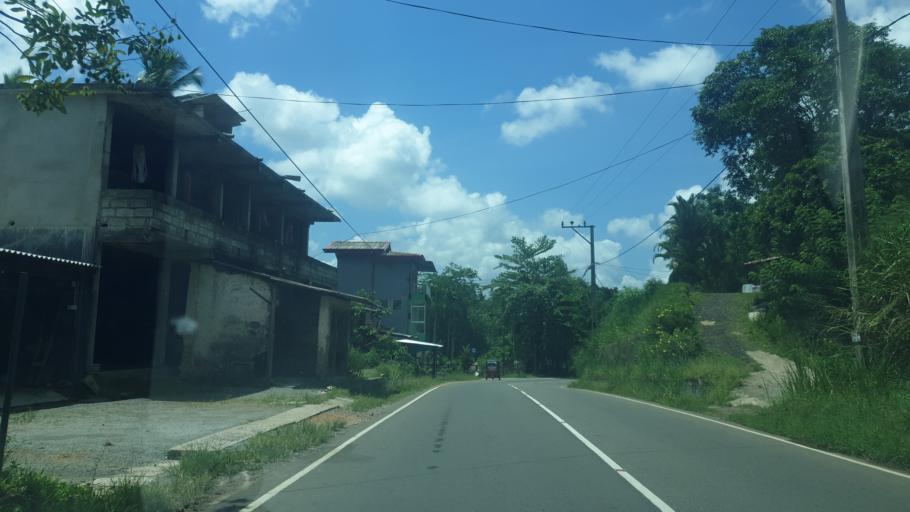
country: LK
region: Western
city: Horawala Junction
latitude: 6.5143
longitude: 80.2424
